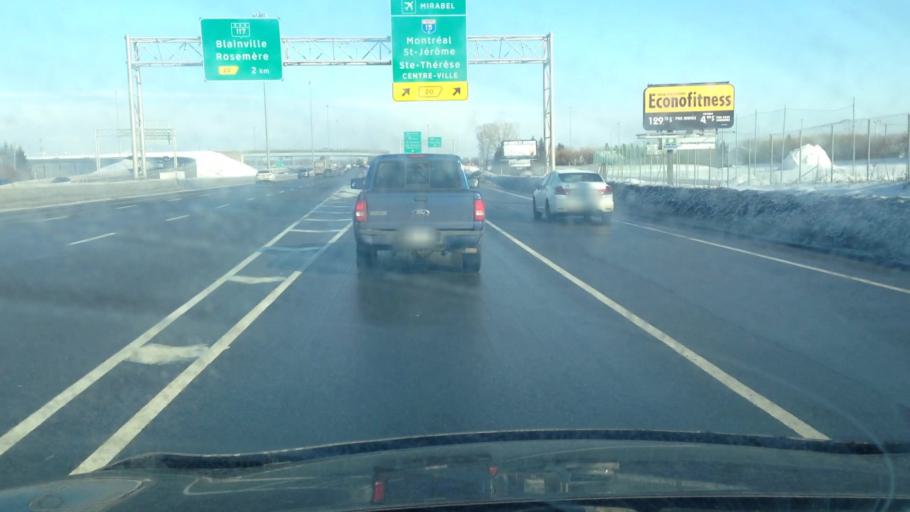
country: CA
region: Quebec
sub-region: Laurentides
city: Boisbriand
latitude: 45.6236
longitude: -73.8455
